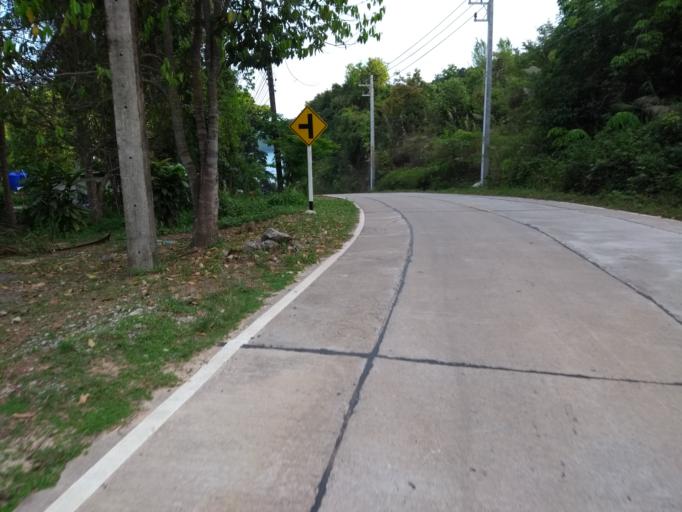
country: TH
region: Trat
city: Ko Kut
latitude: 11.6293
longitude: 102.5462
